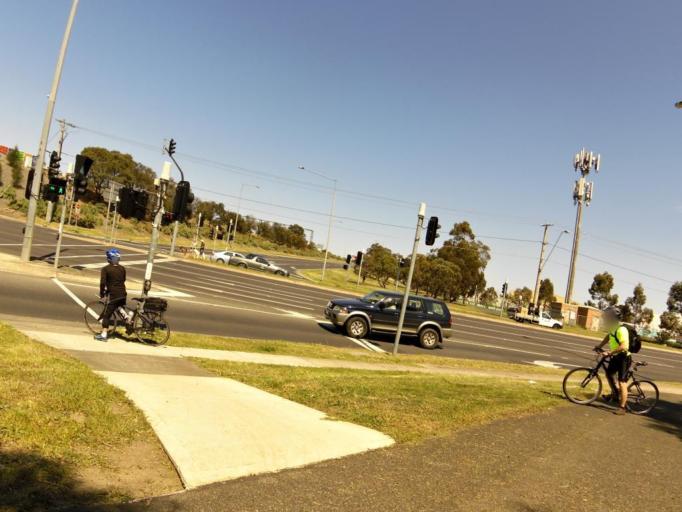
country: AU
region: Victoria
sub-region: Brimbank
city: Sunshine North
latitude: -37.7610
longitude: 144.8201
